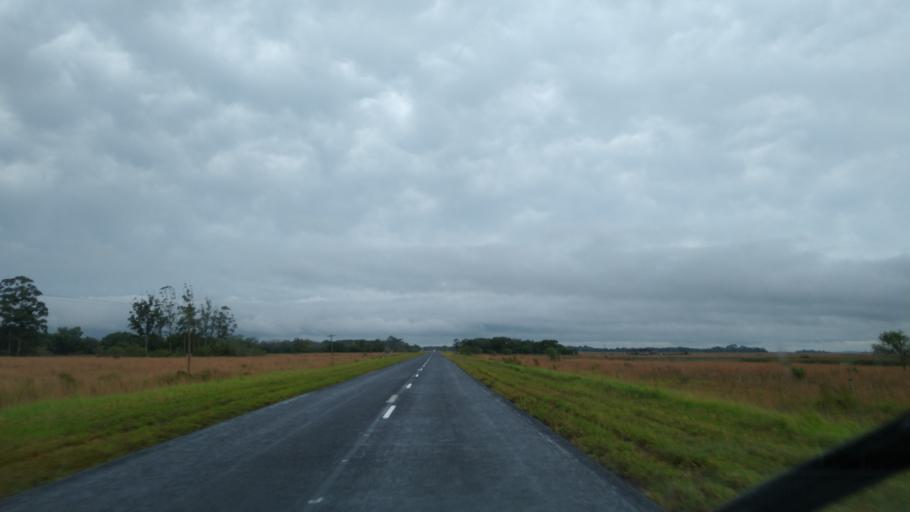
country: AR
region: Corrientes
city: Loreto
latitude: -27.7644
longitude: -57.2663
